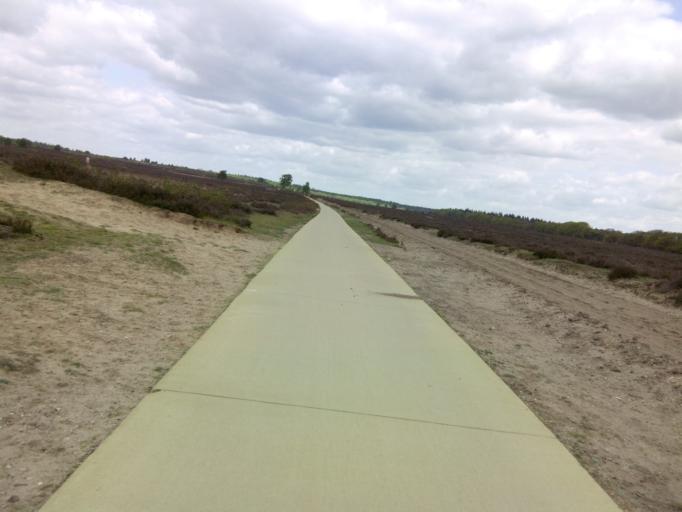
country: NL
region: Gelderland
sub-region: Gemeente Renkum
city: Renkum
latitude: 52.0399
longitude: 5.7255
